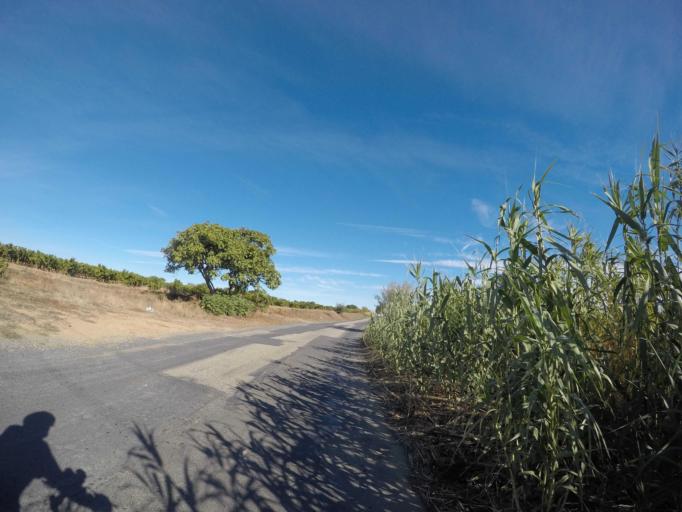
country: FR
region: Languedoc-Roussillon
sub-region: Departement des Pyrenees-Orientales
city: Trouillas
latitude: 42.5993
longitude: 2.8071
